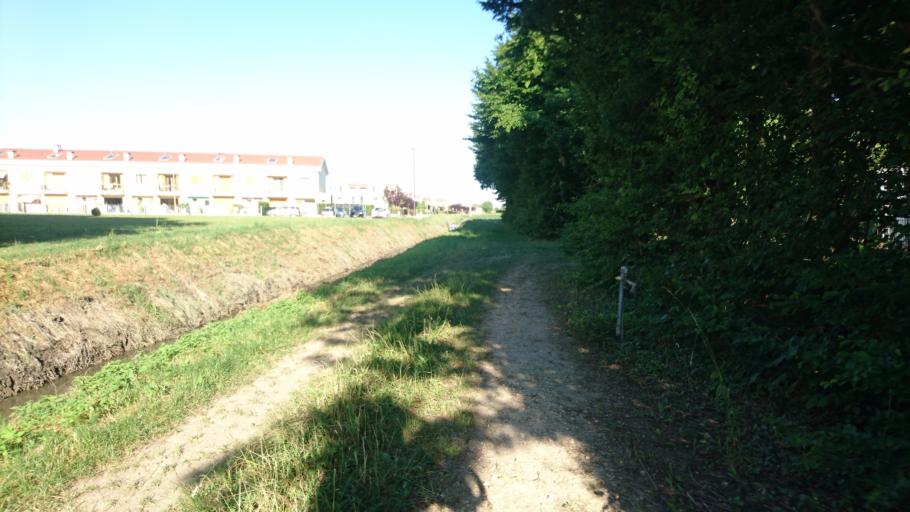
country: IT
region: Veneto
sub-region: Provincia di Padova
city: Ponte San Nicolo
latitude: 45.3635
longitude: 11.9238
